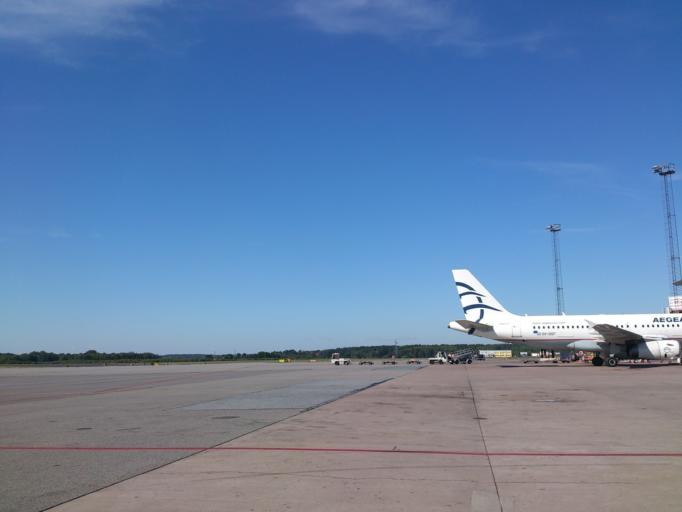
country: SE
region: Stockholm
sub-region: Sigtuna Kommun
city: Marsta
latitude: 59.6503
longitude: 17.9281
